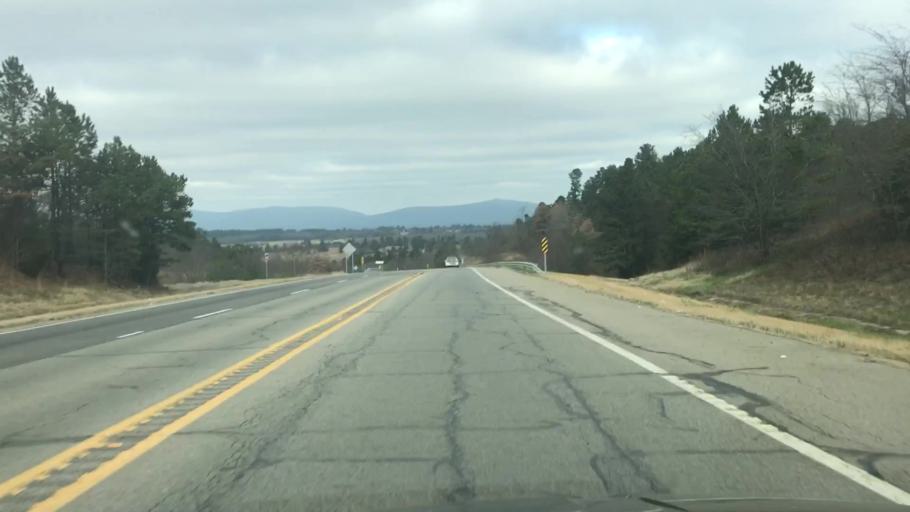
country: US
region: Arkansas
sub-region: Scott County
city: Waldron
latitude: 34.8639
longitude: -94.0734
